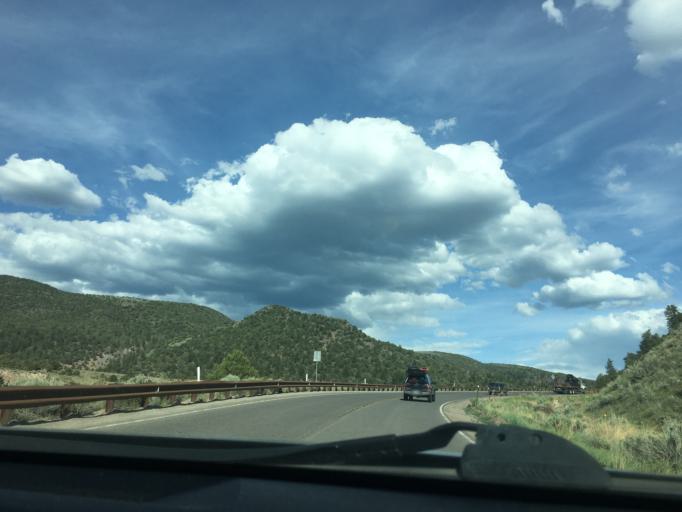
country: US
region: Colorado
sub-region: Eagle County
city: Edwards
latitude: 39.8566
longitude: -106.6478
